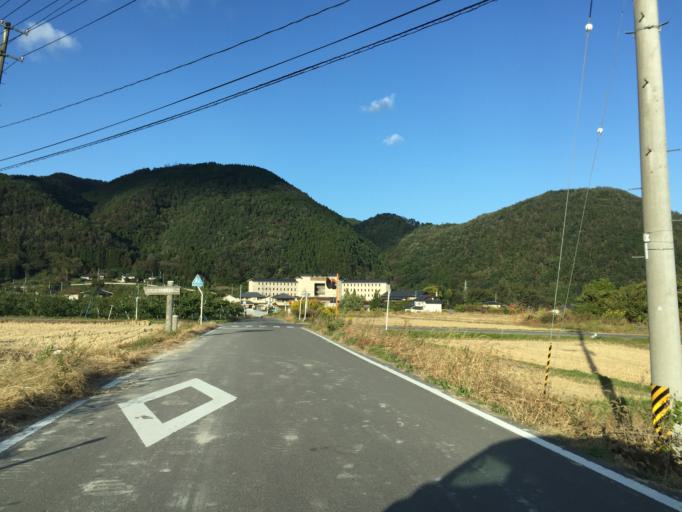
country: JP
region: Fukushima
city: Fukushima-shi
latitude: 37.8375
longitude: 140.4410
